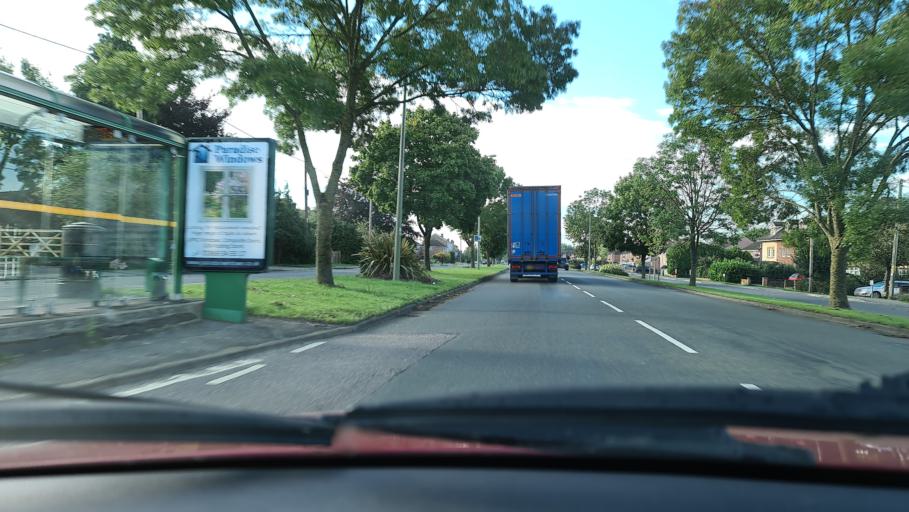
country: GB
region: England
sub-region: Oxfordshire
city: Kidlington
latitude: 51.8143
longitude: -1.2810
